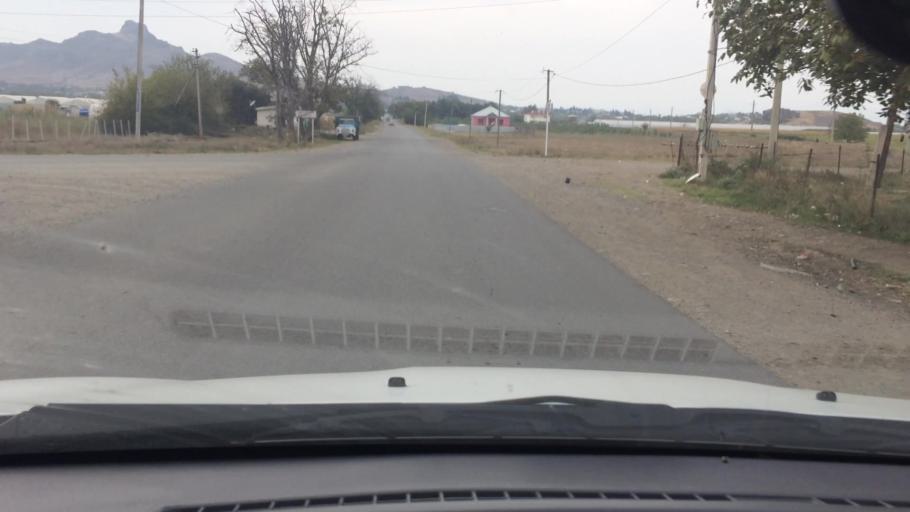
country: GE
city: Naghvarevi
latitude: 41.3549
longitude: 44.8583
